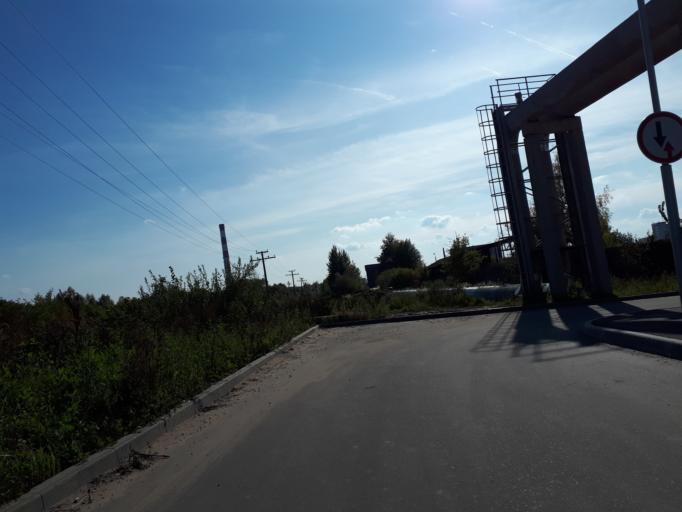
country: BY
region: Vitebsk
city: Vitebsk
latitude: 55.1637
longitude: 30.2444
